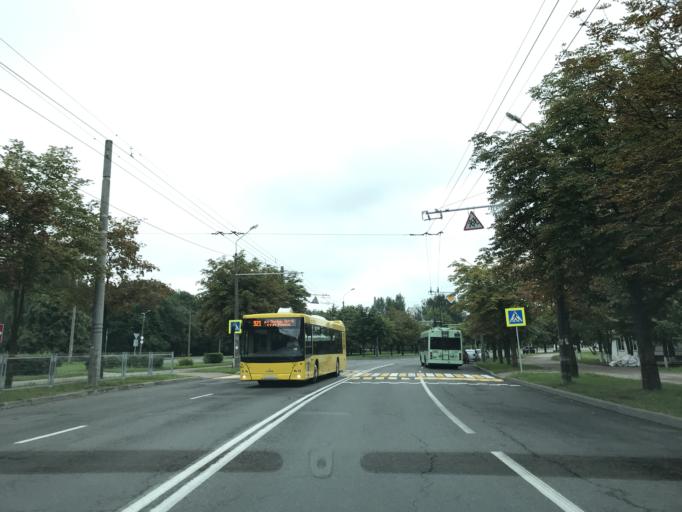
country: BY
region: Minsk
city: Borovlyany
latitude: 53.9498
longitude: 27.6401
